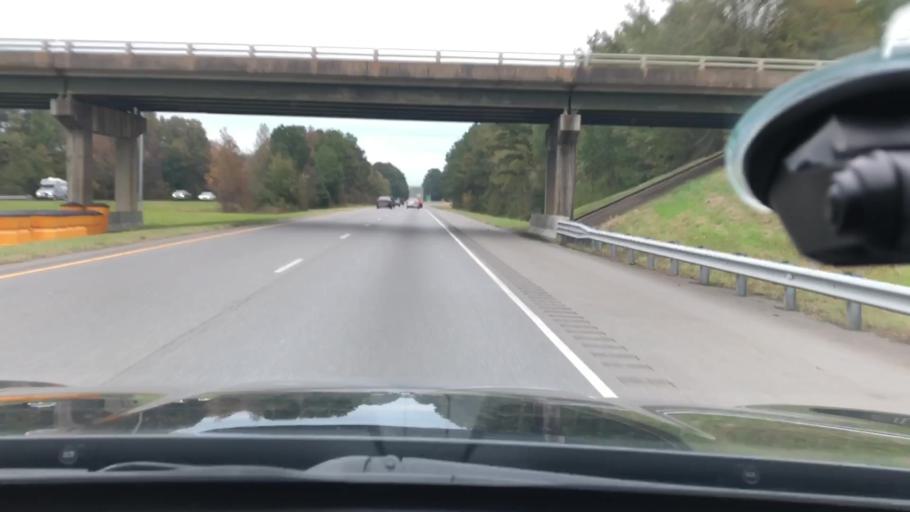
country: US
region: Arkansas
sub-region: Hempstead County
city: Hope
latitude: 33.6468
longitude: -93.6801
